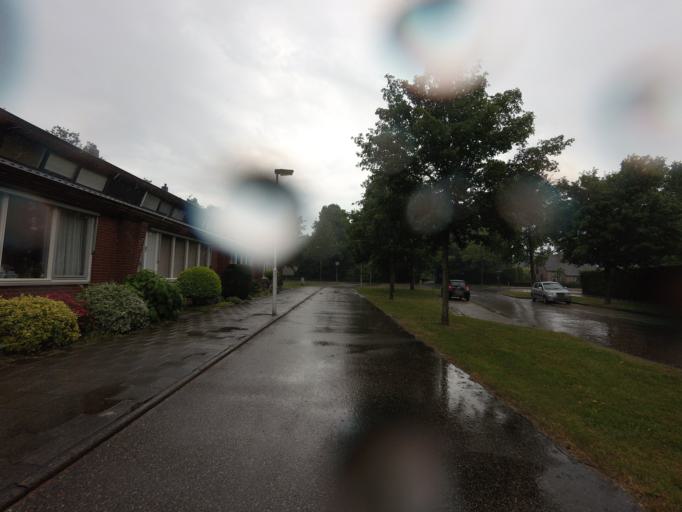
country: NL
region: Utrecht
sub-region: Stichtse Vecht
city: Spechtenkamp
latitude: 52.1059
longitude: 5.0171
